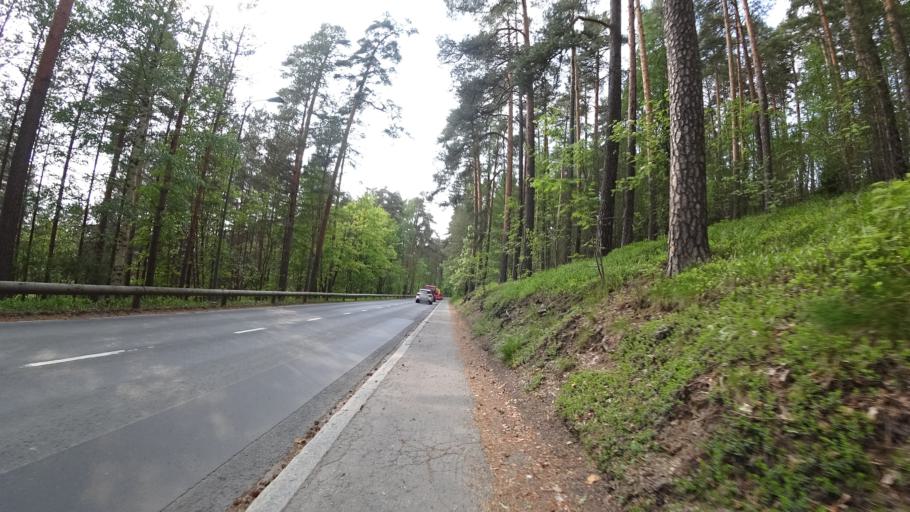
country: FI
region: Pirkanmaa
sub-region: Tampere
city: Tampere
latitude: 61.4933
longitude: 23.7391
